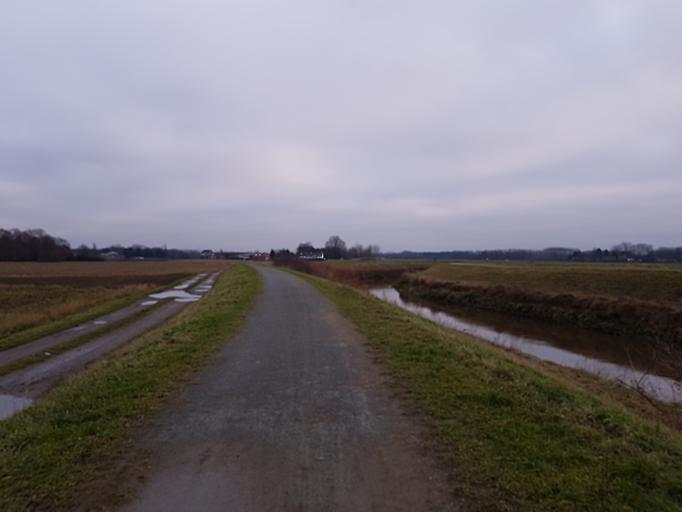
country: BE
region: Flanders
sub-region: Provincie Vlaams-Brabant
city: Haacht
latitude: 50.9890
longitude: 4.6640
